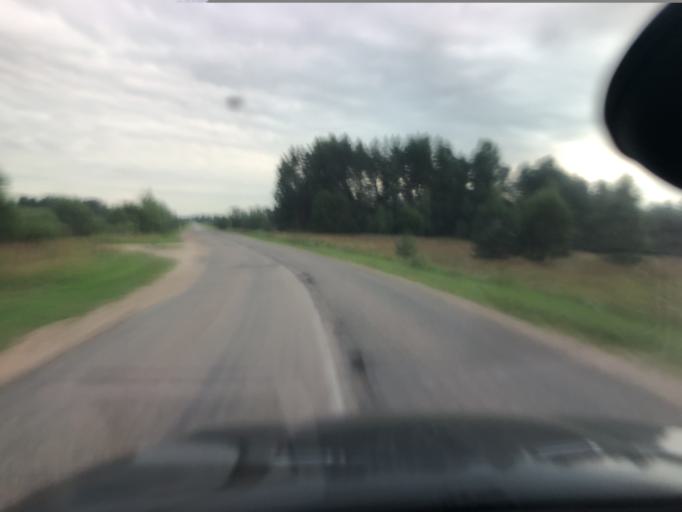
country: RU
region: Jaroslavl
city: Petrovsk
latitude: 57.0036
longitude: 39.0233
